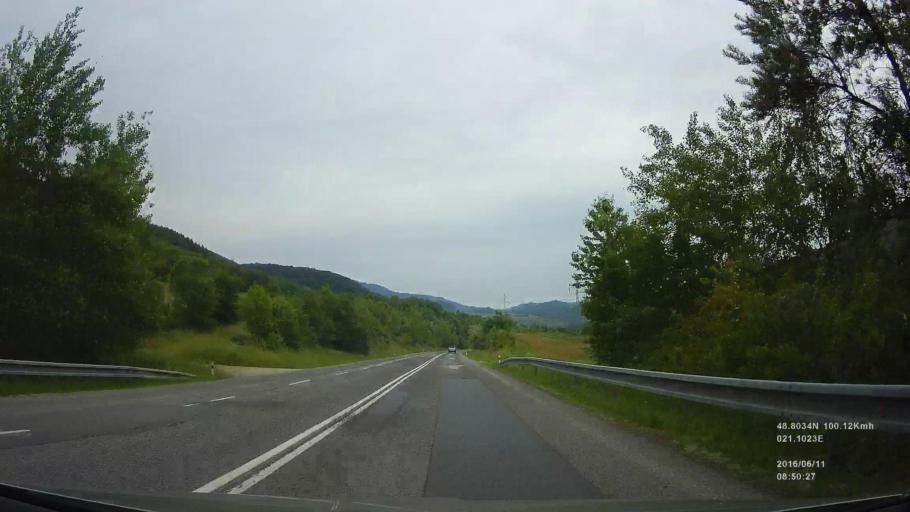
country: SK
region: Kosicky
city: Kosice
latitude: 48.7978
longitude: 21.1119
